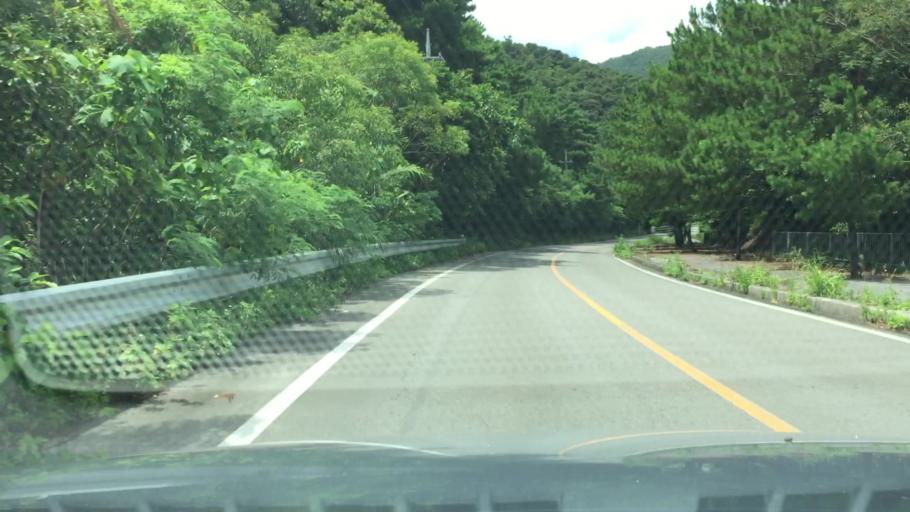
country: JP
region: Okinawa
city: Ishigaki
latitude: 24.4314
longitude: 124.2102
